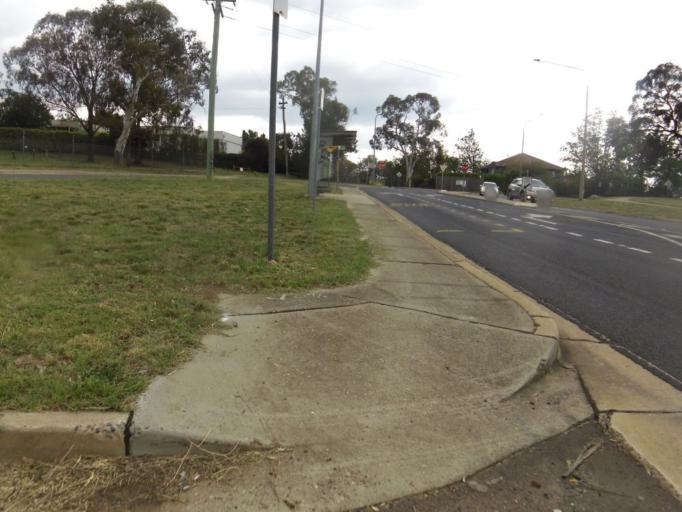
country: AU
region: Australian Capital Territory
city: Forrest
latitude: -35.3431
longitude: 149.1385
